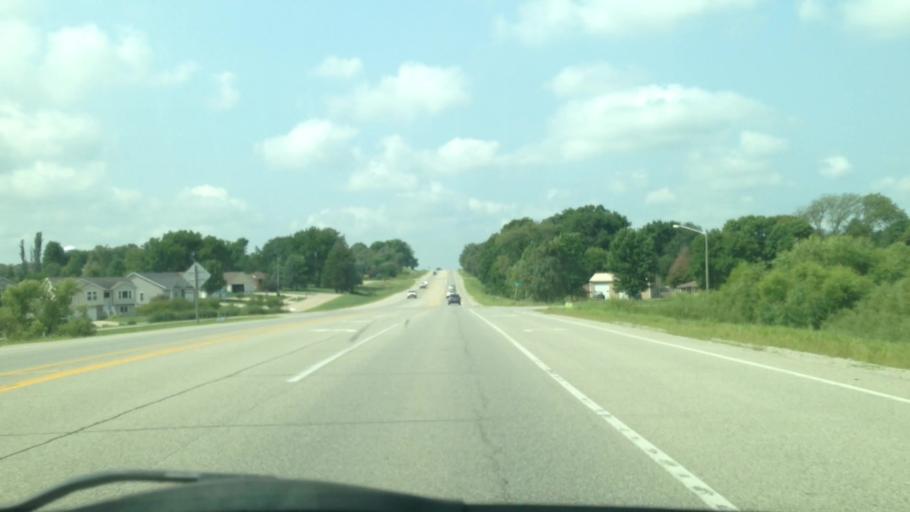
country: US
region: Iowa
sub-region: Linn County
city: Fairfax
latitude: 41.9383
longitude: -91.7575
